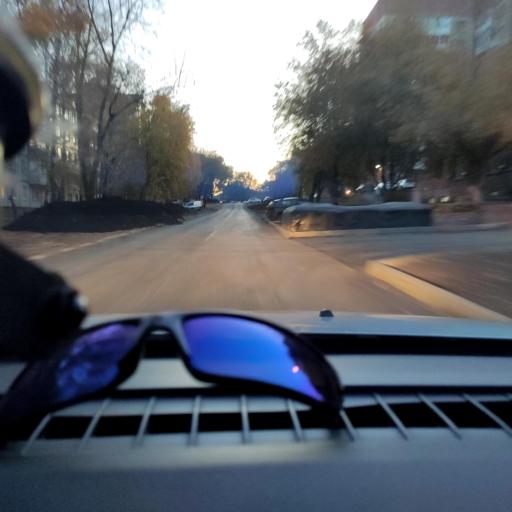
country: RU
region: Samara
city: Samara
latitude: 53.2202
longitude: 50.2218
